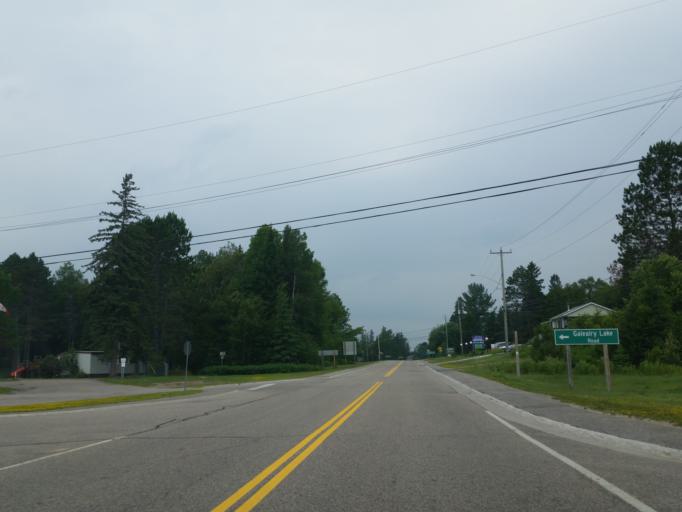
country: CA
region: Ontario
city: Bancroft
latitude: 45.4948
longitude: -78.2400
